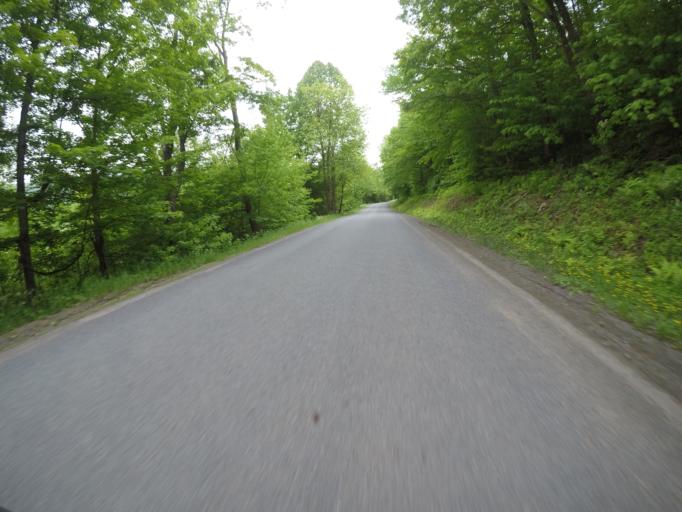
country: US
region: New York
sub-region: Delaware County
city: Stamford
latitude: 42.2416
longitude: -74.7062
